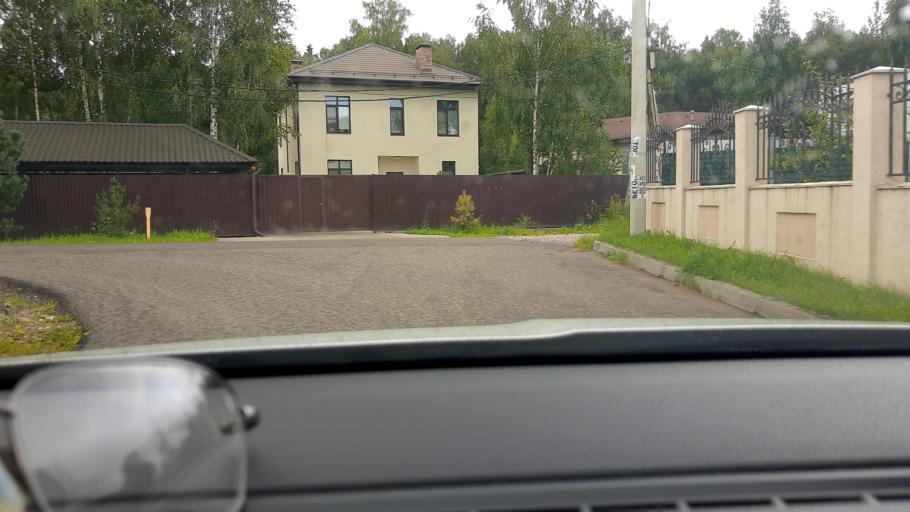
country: RU
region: Moskovskaya
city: Dolgoprudnyy
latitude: 55.9447
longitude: 37.4568
